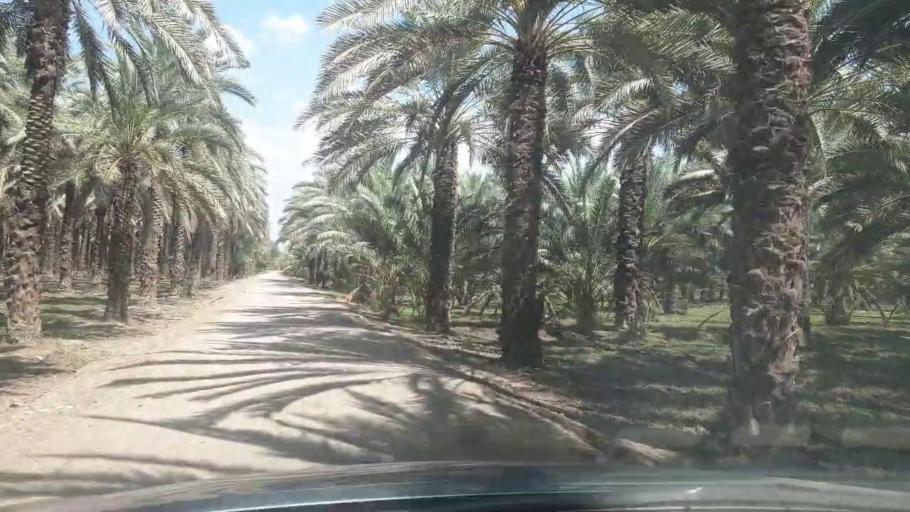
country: PK
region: Sindh
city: Khairpur
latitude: 27.5502
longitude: 68.7926
